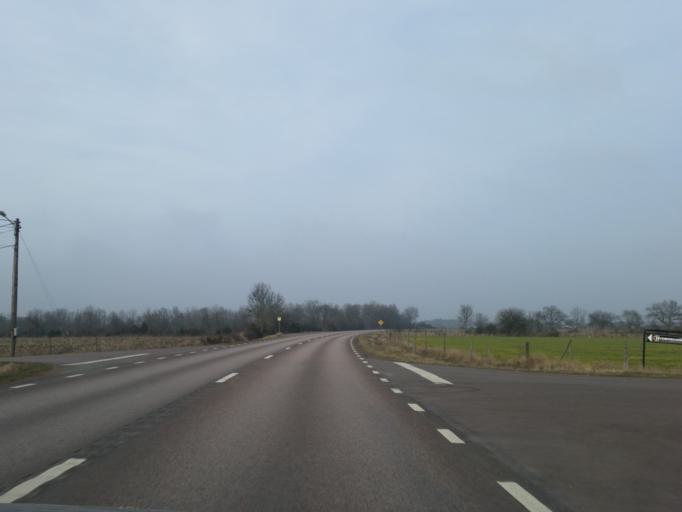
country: SE
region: Kalmar
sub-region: Borgholms Kommun
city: Borgholm
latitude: 57.1298
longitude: 16.9725
